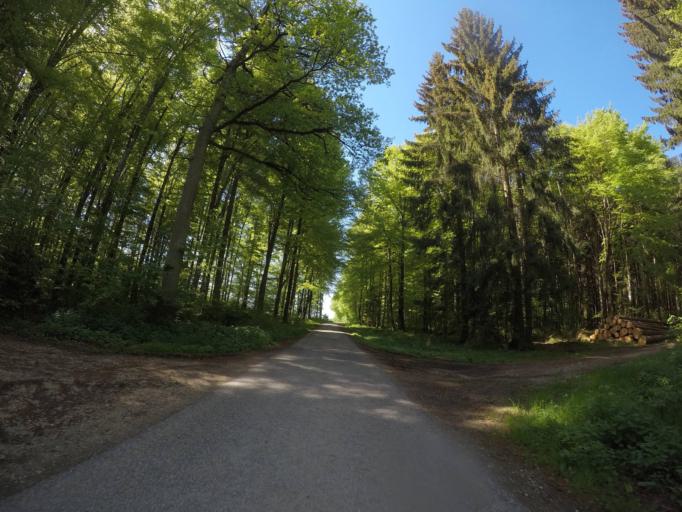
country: DE
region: Baden-Wuerttemberg
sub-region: Tuebingen Region
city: Laichingen
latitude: 48.4428
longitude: 9.7080
